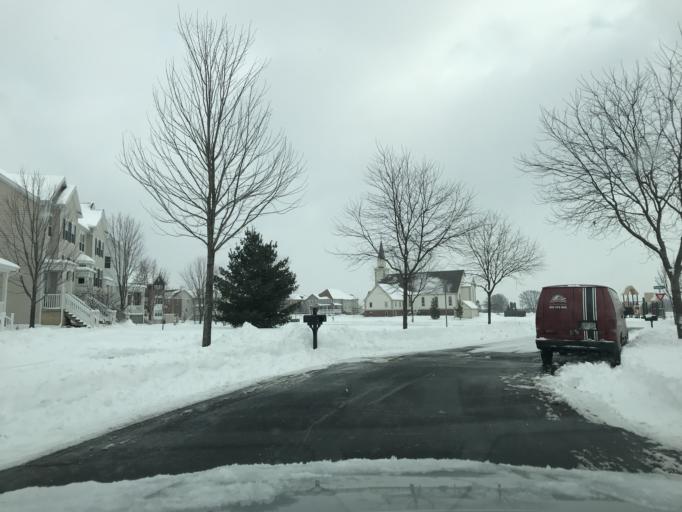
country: US
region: Wisconsin
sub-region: Dane County
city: Sun Prairie
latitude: 43.1668
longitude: -89.2809
